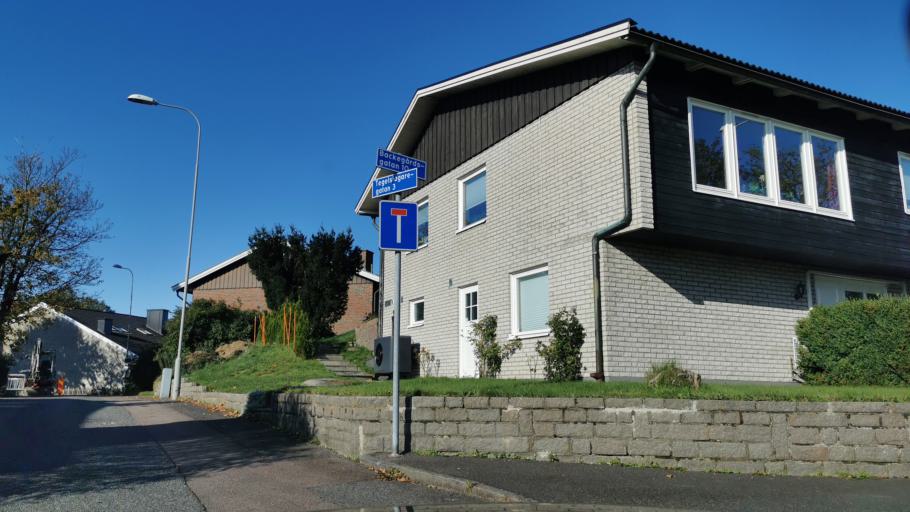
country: SE
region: Vaestra Goetaland
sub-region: Goteborg
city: Eriksbo
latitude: 57.7379
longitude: 12.0551
